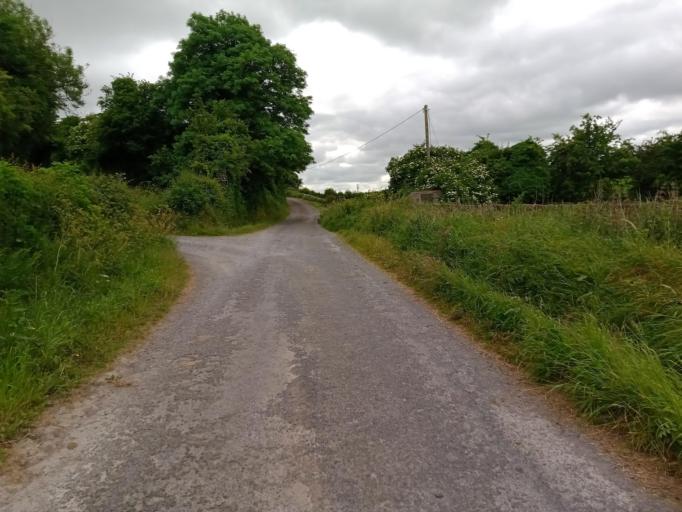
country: IE
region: Leinster
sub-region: Laois
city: Rathdowney
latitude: 52.7874
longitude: -7.4796
